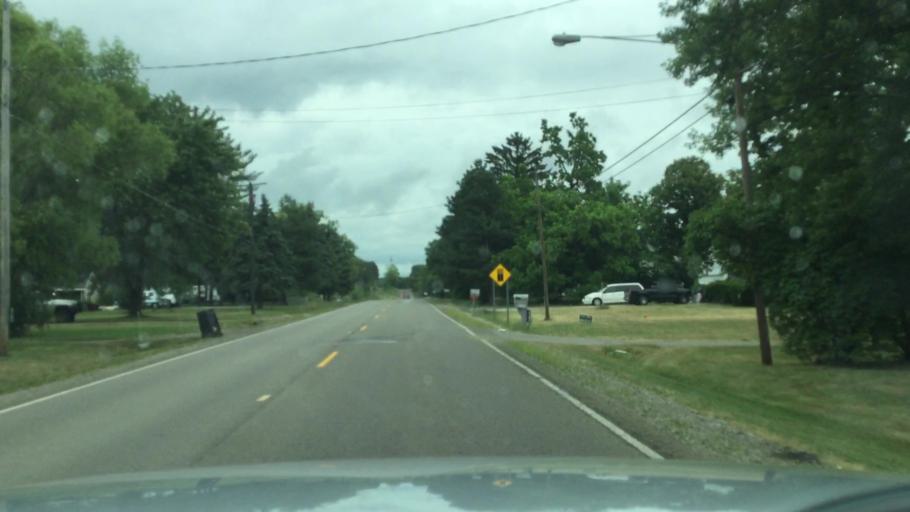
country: US
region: Michigan
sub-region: Genesee County
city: Beecher
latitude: 43.0814
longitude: -83.6366
